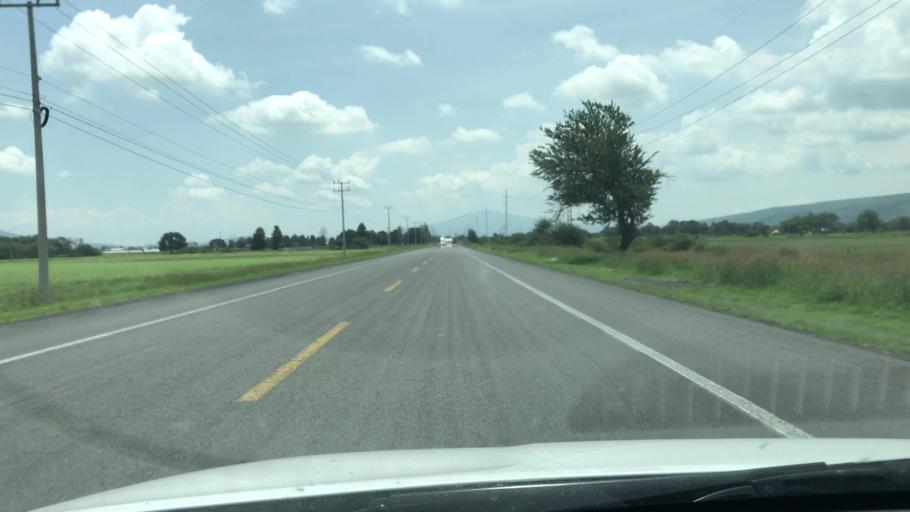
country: MX
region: Michoacan
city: Tanhuato de Guerrero
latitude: 20.2807
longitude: -102.3578
